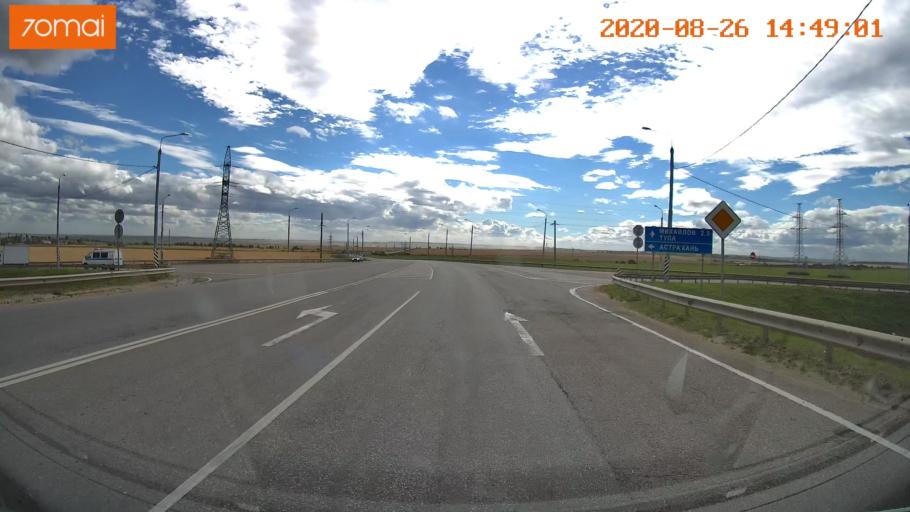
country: RU
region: Rjazan
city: Mikhaylov
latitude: 54.2615
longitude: 39.0044
